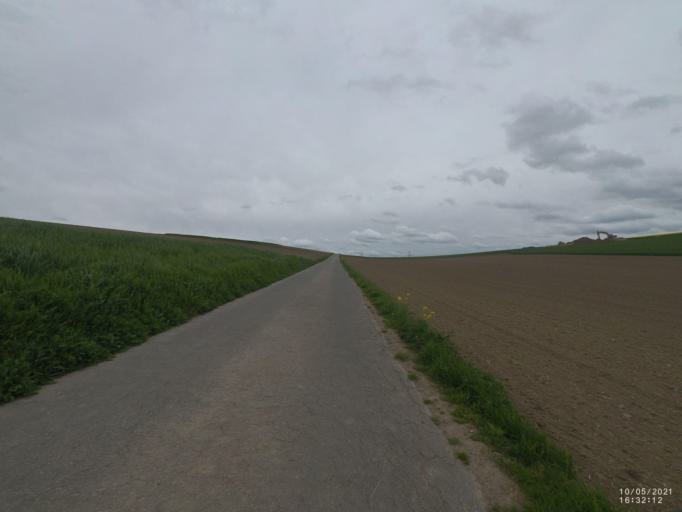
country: DE
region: Rheinland-Pfalz
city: Ruber
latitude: 50.3071
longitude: 7.3682
